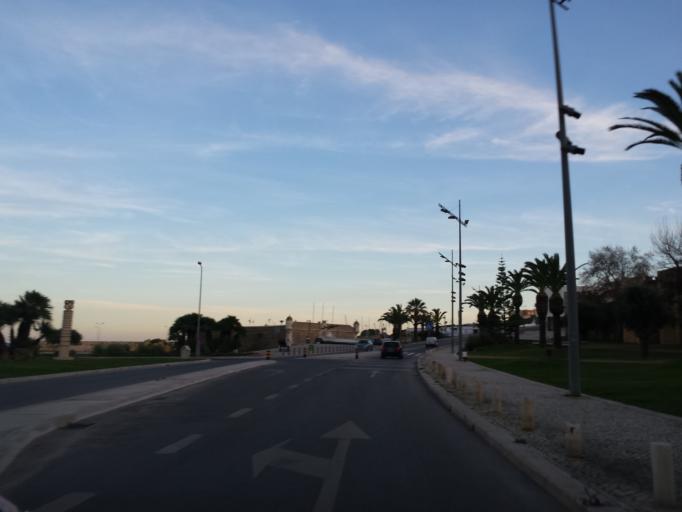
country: PT
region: Faro
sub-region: Lagos
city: Lagos
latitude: 37.1002
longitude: -8.6694
